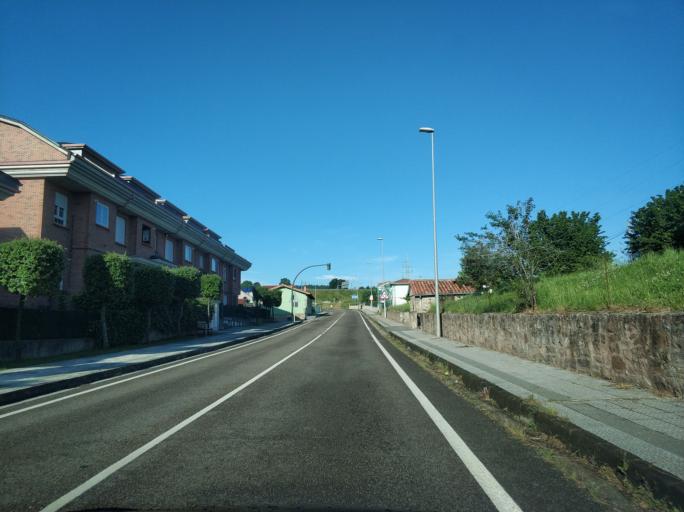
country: ES
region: Cantabria
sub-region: Provincia de Cantabria
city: Polanco
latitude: 43.3463
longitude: -3.9921
